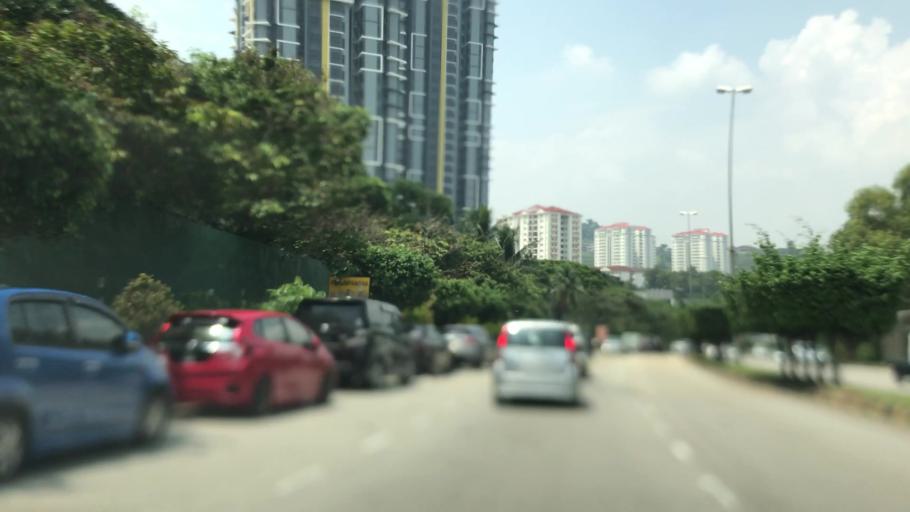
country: MY
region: Selangor
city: Subang Jaya
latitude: 3.0232
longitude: 101.6226
